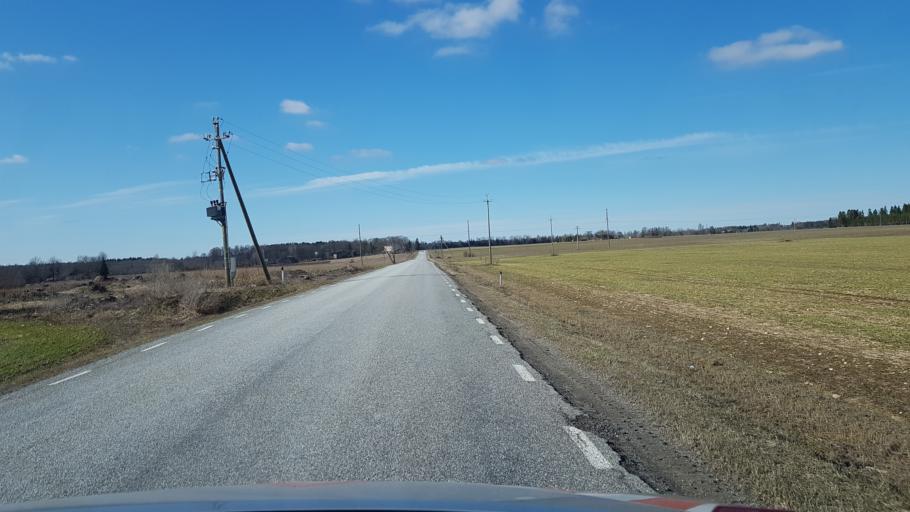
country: EE
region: Laeaene-Virumaa
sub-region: Tapa vald
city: Tapa
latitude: 59.2654
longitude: 26.0144
